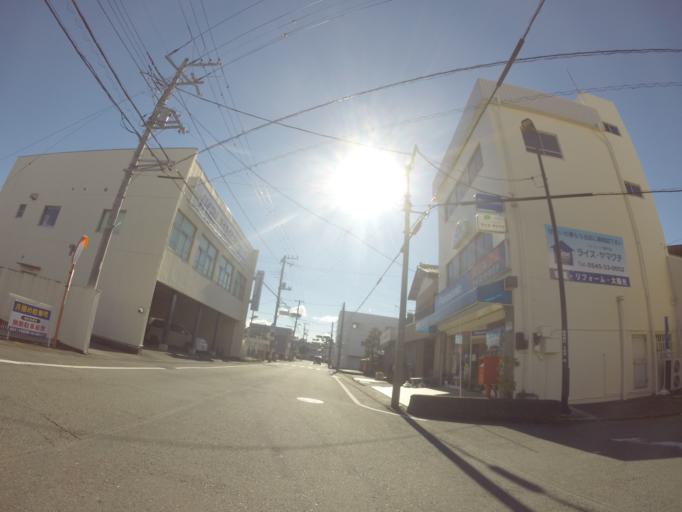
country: JP
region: Shizuoka
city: Fuji
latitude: 35.1450
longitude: 138.7040
